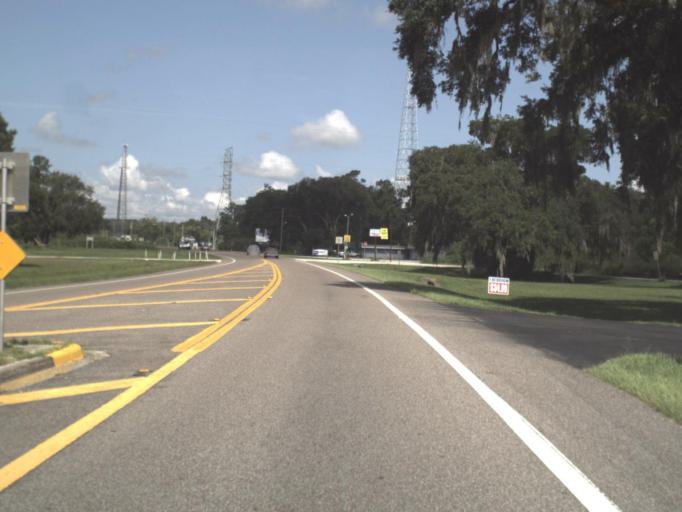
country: US
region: Florida
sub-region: Hernando County
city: Brooksville
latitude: 28.5451
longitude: -82.3711
